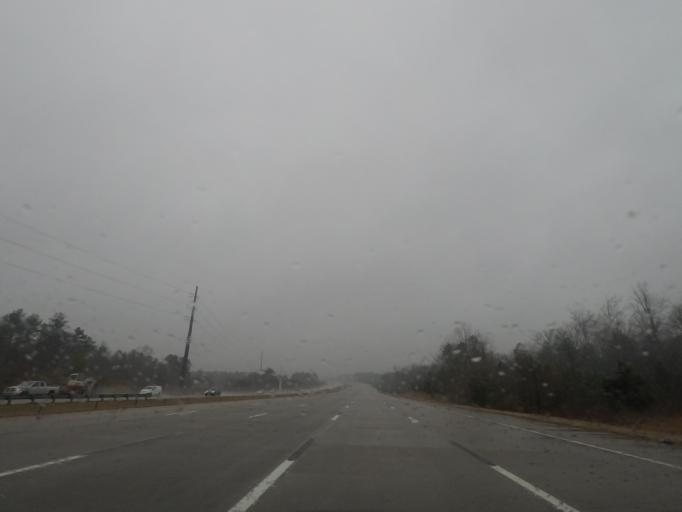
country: US
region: North Carolina
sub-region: Wake County
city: Morrisville
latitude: 35.8462
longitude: -78.8739
